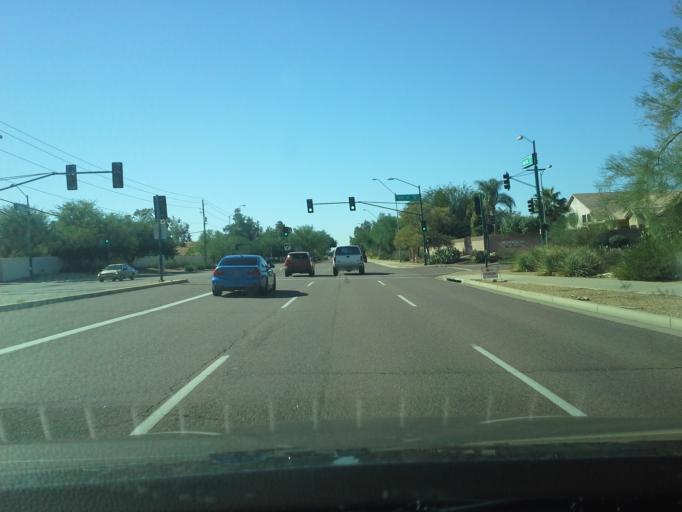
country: US
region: Arizona
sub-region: Maricopa County
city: Paradise Valley
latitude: 33.6405
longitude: -111.9509
